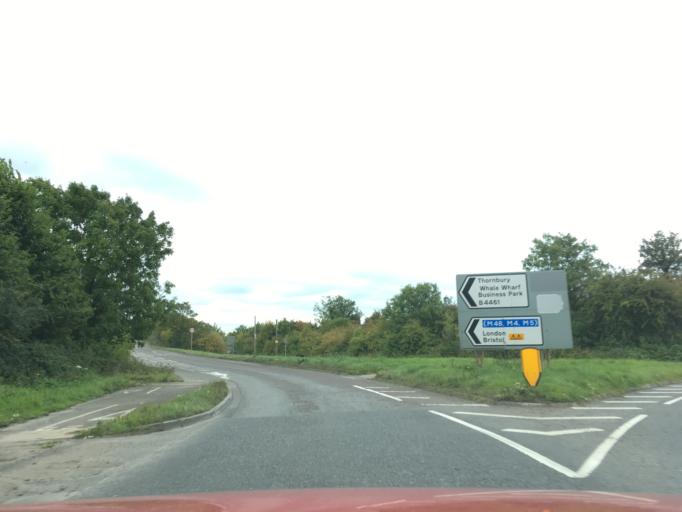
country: GB
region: England
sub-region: South Gloucestershire
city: Severn Beach
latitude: 51.6016
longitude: -2.6164
